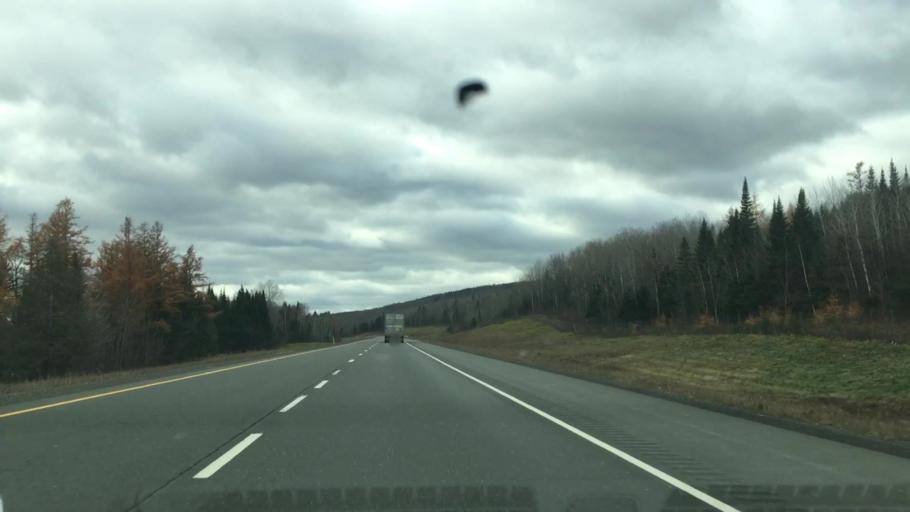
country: US
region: Maine
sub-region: Aroostook County
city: Fort Fairfield
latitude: 46.6562
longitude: -67.7361
